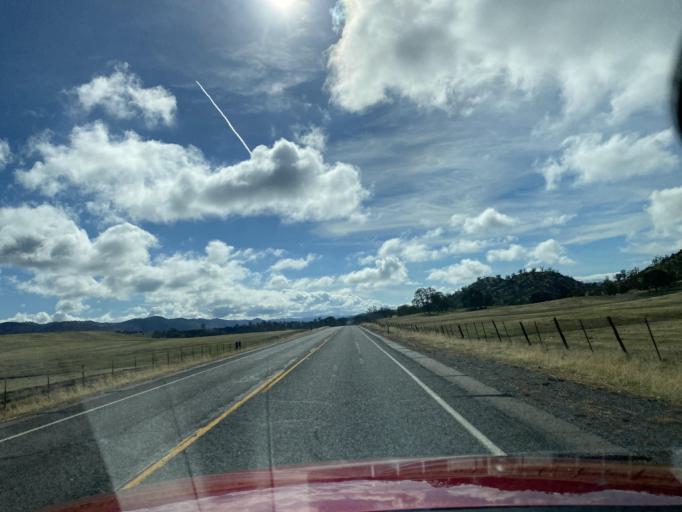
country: US
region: California
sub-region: Glenn County
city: Willows
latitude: 39.5280
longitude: -122.5320
